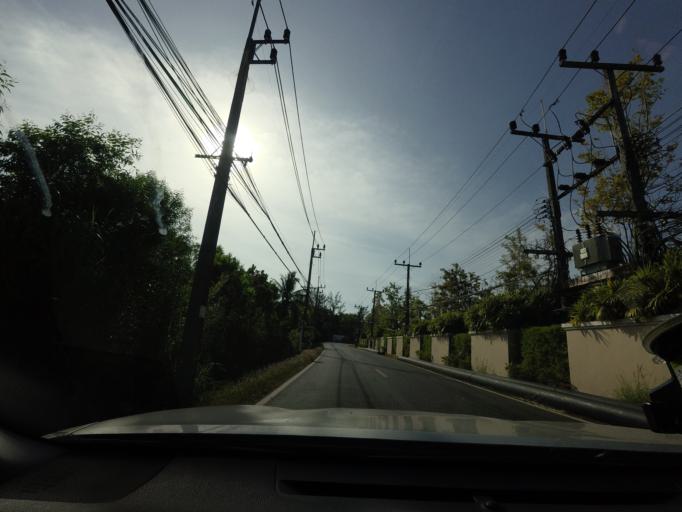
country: TH
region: Phuket
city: Thalang
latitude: 8.0193
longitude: 98.3024
